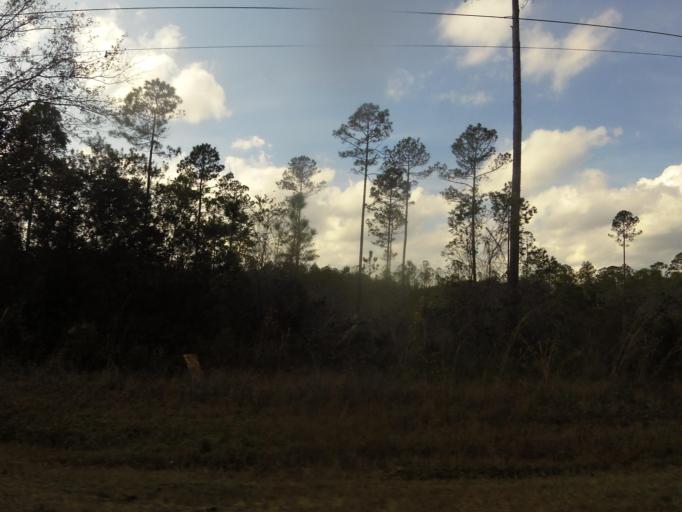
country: US
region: Florida
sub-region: Duval County
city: Baldwin
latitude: 30.2025
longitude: -81.9912
